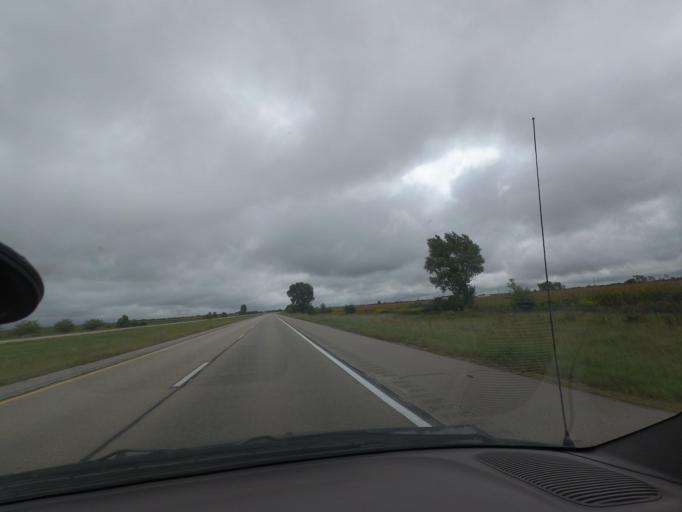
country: US
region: Illinois
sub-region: Piatt County
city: Monticello
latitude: 40.0294
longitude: -88.6508
